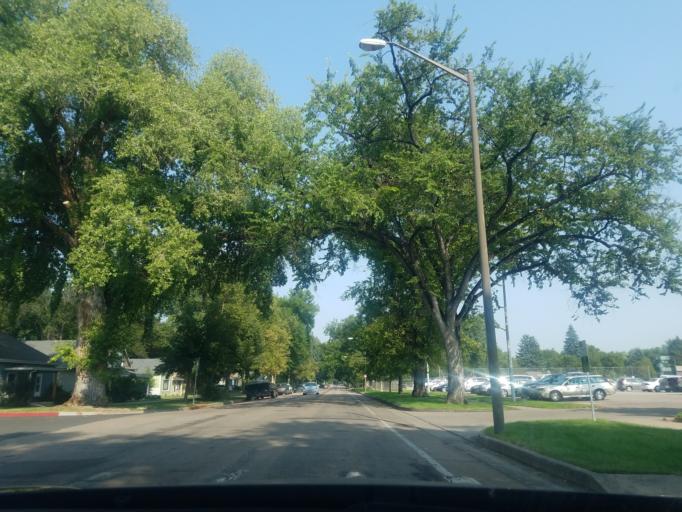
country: US
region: Colorado
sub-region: Larimer County
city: Fort Collins
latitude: 40.5710
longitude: -105.0744
